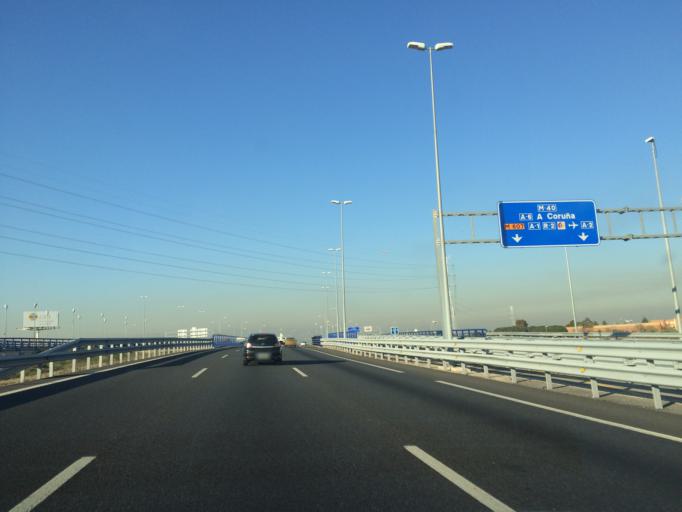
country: ES
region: Madrid
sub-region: Provincia de Madrid
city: Pozuelo de Alarcon
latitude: 40.3956
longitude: -3.8328
